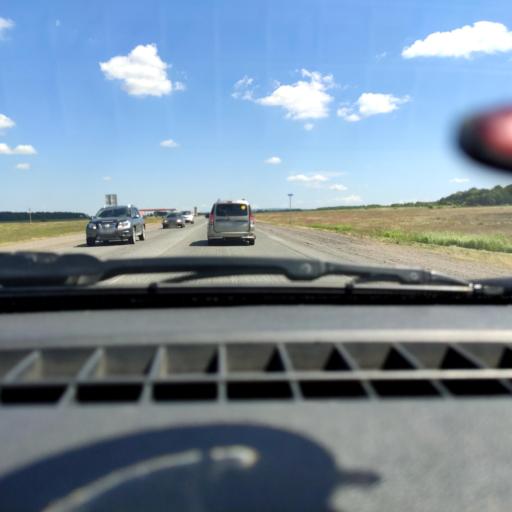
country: RU
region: Bashkortostan
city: Kudeyevskiy
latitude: 54.8174
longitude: 56.8000
